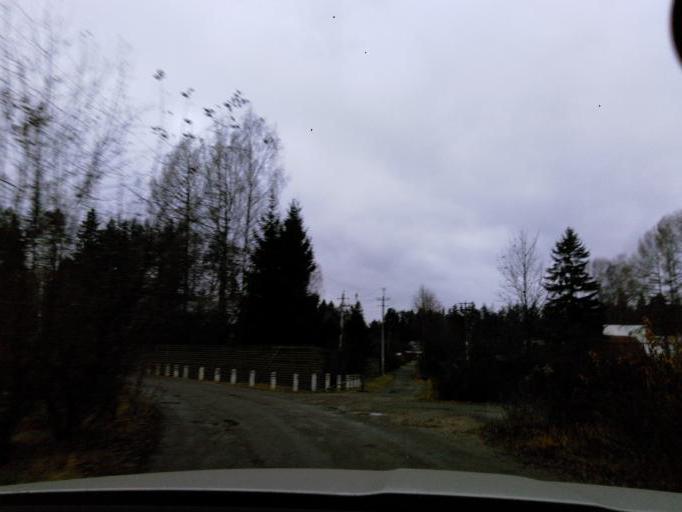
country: RU
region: Moskovskaya
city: Lozhki
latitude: 56.0543
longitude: 37.0979
